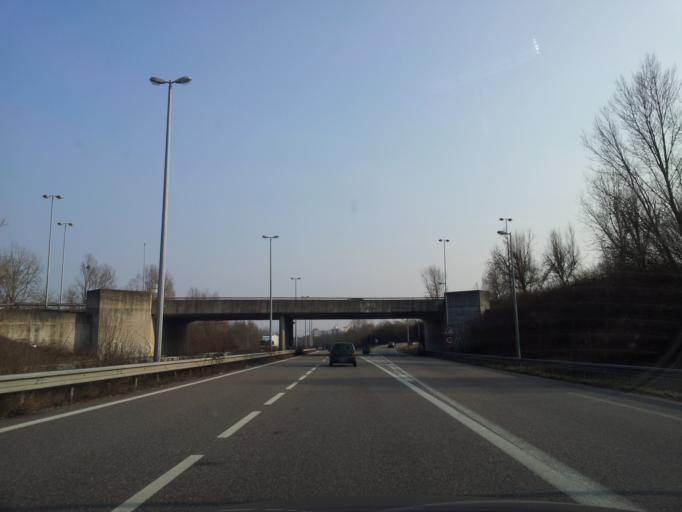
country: FR
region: Alsace
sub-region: Departement du Haut-Rhin
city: Saint-Louis
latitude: 47.5894
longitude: 7.5463
